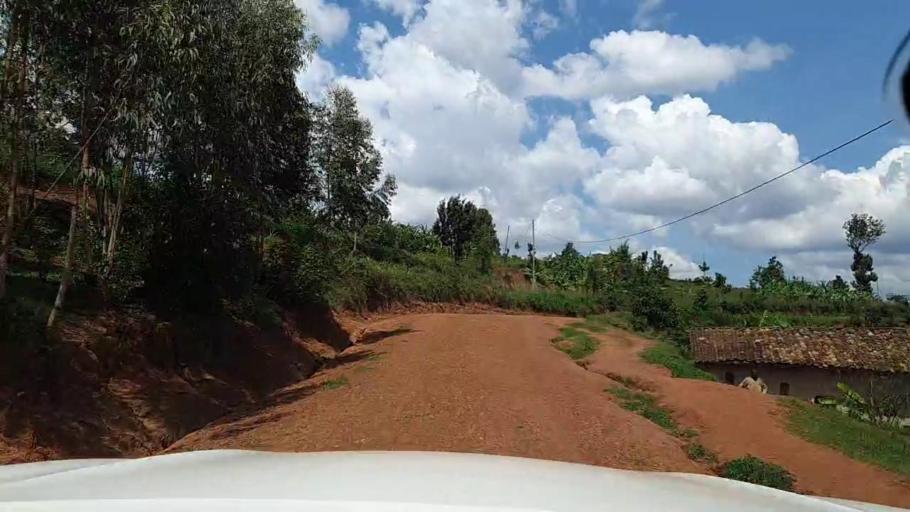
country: RW
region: Southern Province
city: Butare
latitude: -2.7476
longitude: 29.7043
